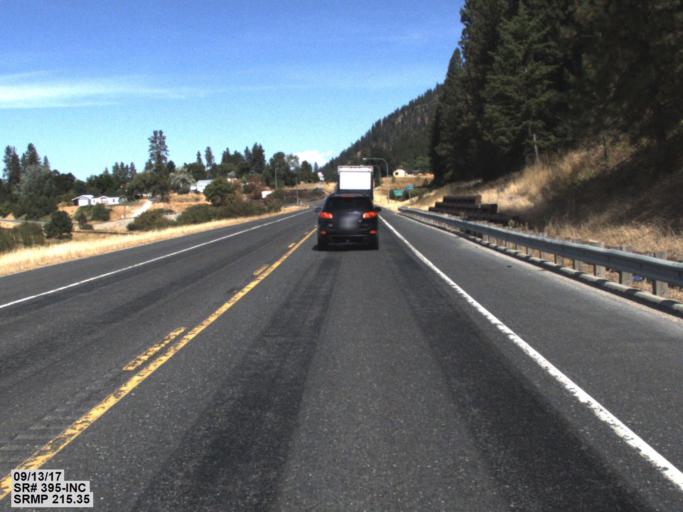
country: US
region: Washington
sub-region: Stevens County
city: Chewelah
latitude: 48.3498
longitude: -117.8334
